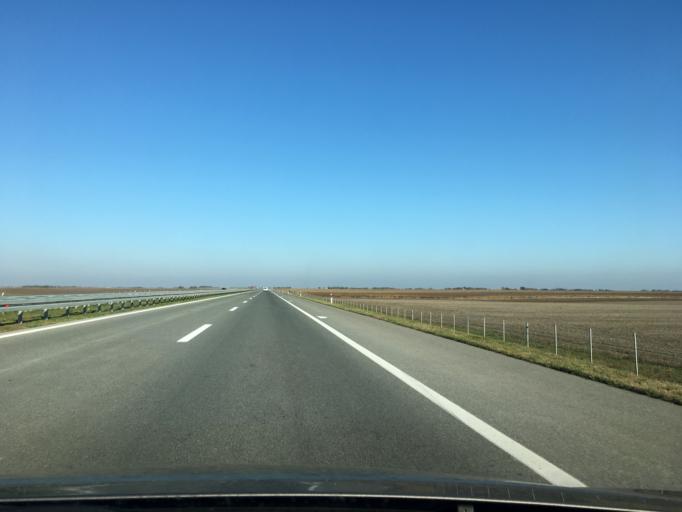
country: RS
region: Autonomna Pokrajina Vojvodina
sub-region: Severnobacki Okrug
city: Mali Igos
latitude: 45.7571
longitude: 19.7018
